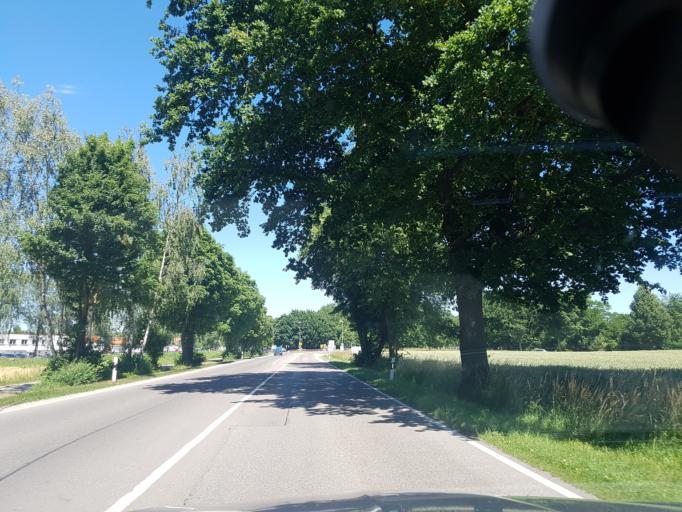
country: DE
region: Bavaria
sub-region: Swabia
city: Weissenhorn
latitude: 48.3004
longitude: 10.1512
